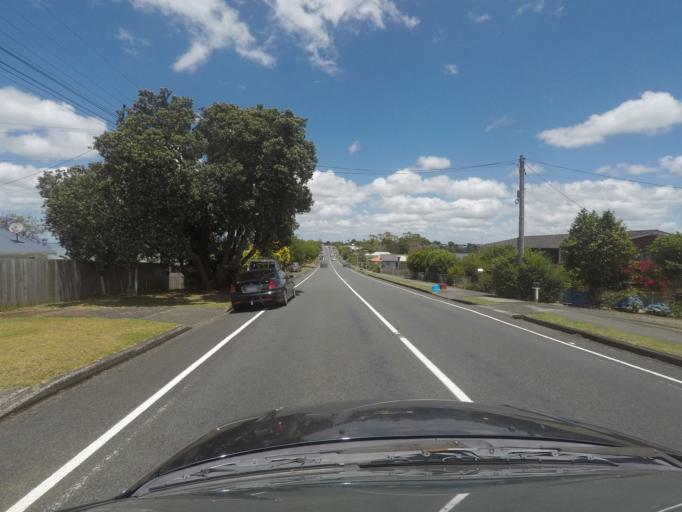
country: NZ
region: Northland
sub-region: Whangarei
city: Whangarei
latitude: -35.7605
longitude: 174.3671
